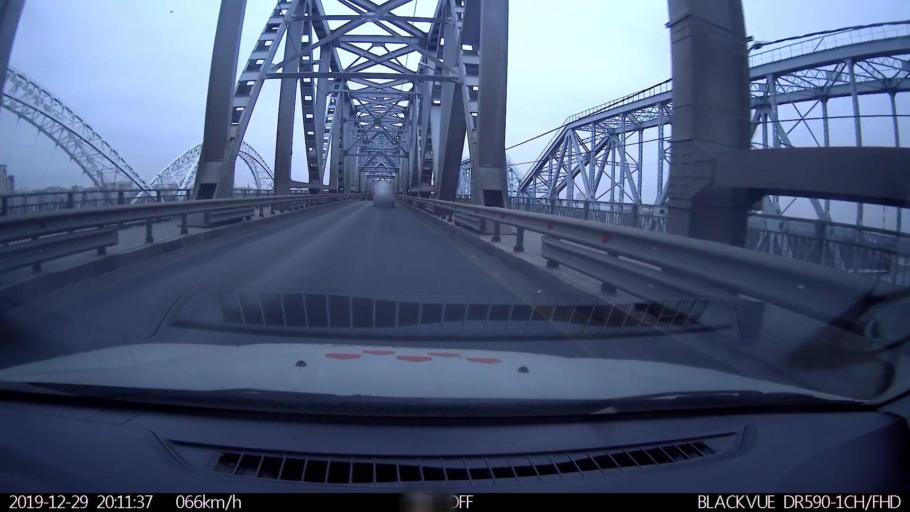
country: RU
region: Nizjnij Novgorod
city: Neklyudovo
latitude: 56.3535
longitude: 43.9244
